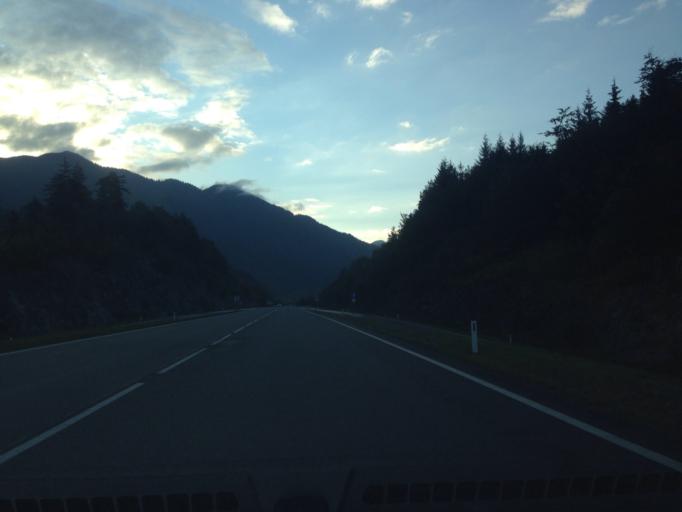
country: AT
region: Tyrol
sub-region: Politischer Bezirk Reutte
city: Pflach
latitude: 47.5247
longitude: 10.7032
